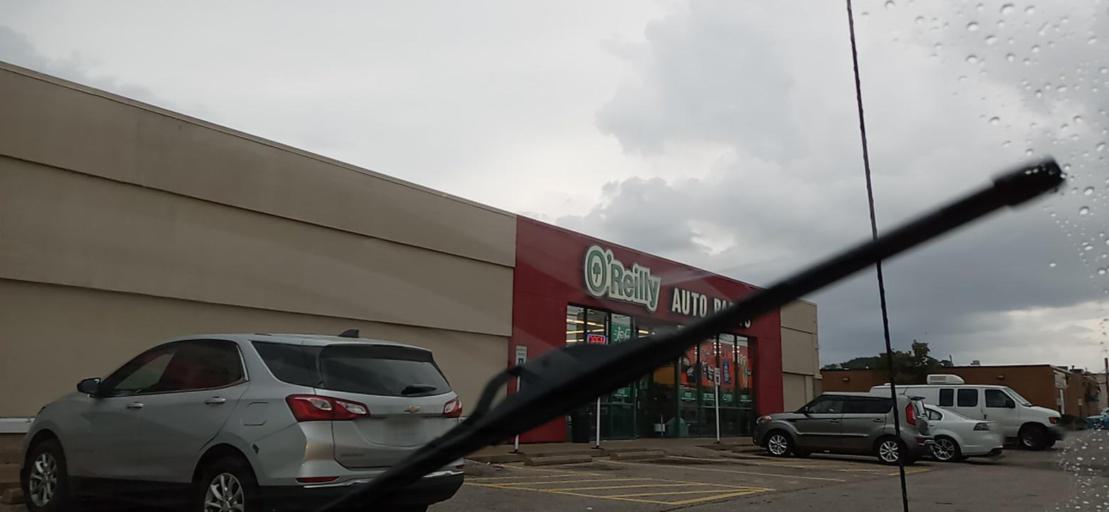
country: US
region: Ohio
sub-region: Summit County
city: Akron
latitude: 41.0658
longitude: -81.5699
